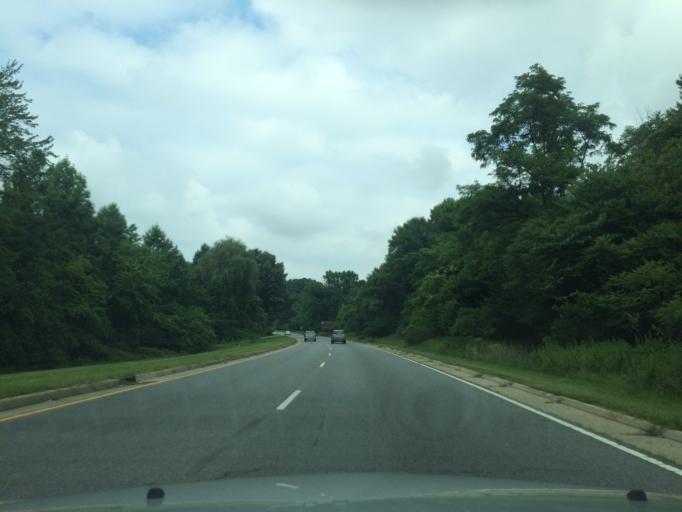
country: US
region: Maryland
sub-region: Prince George's County
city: Silver Hill
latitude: 38.8505
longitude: -76.9455
